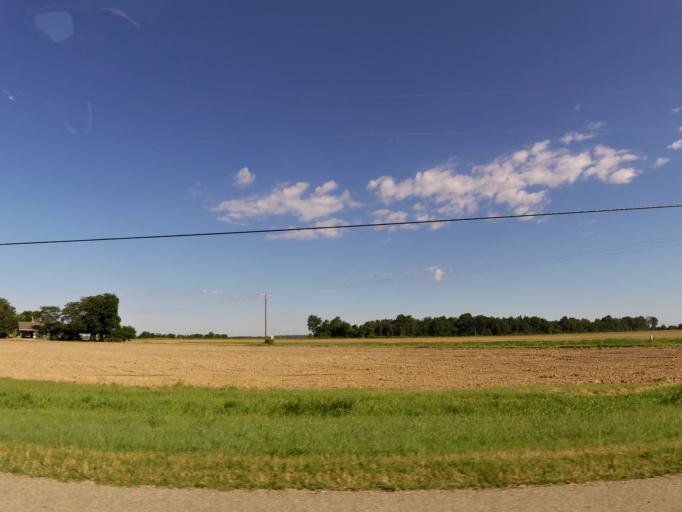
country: US
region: Arkansas
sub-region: Clay County
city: Corning
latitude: 36.4672
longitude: -90.5683
